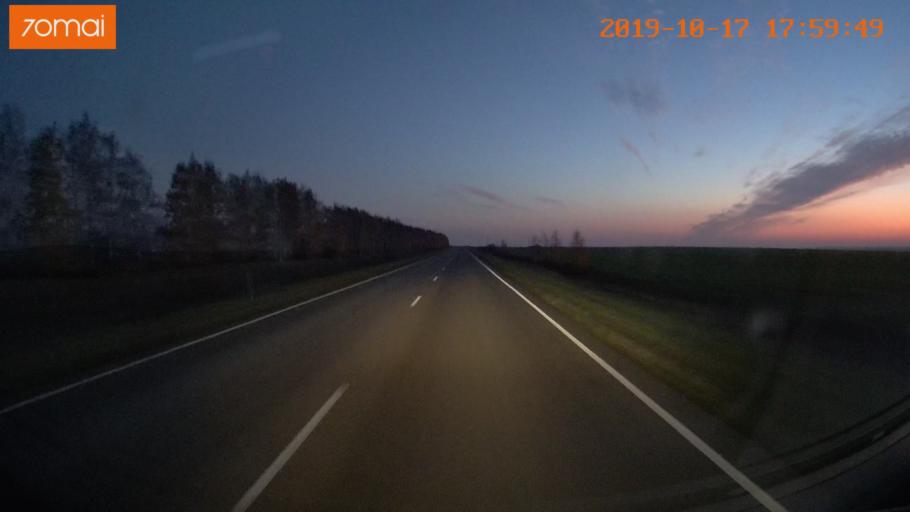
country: RU
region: Tula
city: Kurkino
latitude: 53.5315
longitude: 38.6196
